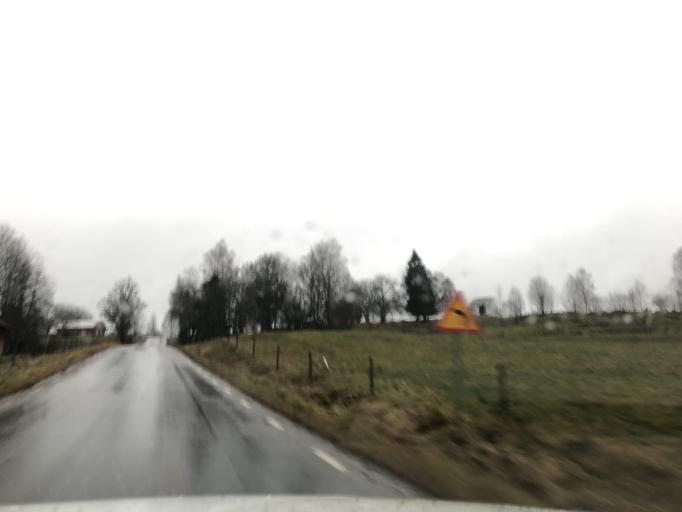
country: SE
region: Vaestra Goetaland
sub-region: Ulricehamns Kommun
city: Ulricehamn
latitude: 57.8500
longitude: 13.5434
